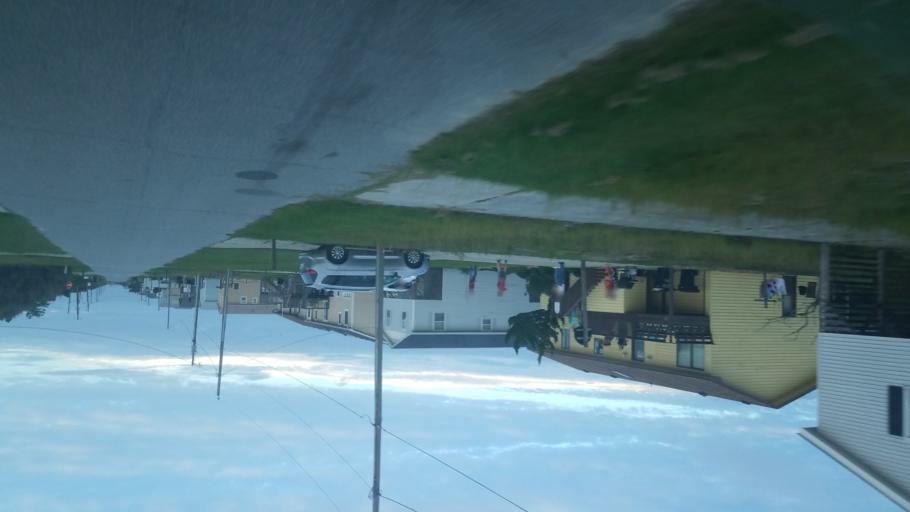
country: US
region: North Carolina
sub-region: Dare County
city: Kitty Hawk
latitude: 36.0902
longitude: -75.7067
